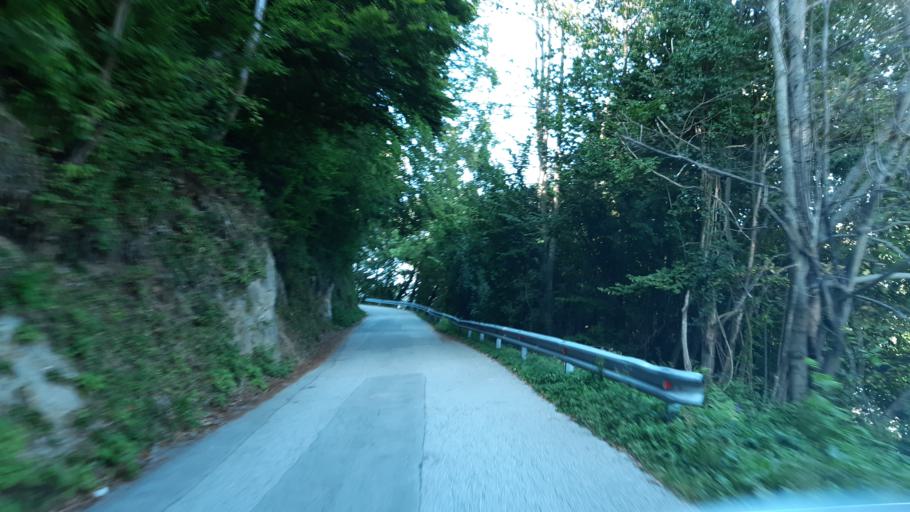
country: SI
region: Kranj
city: Kranj
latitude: 46.2426
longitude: 14.3377
